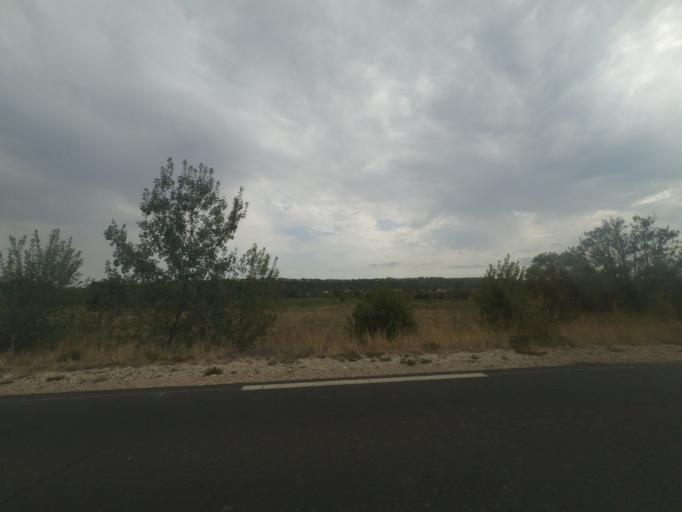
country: FR
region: Languedoc-Roussillon
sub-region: Departement de l'Herault
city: Les Matelles
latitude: 43.7331
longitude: 3.8218
